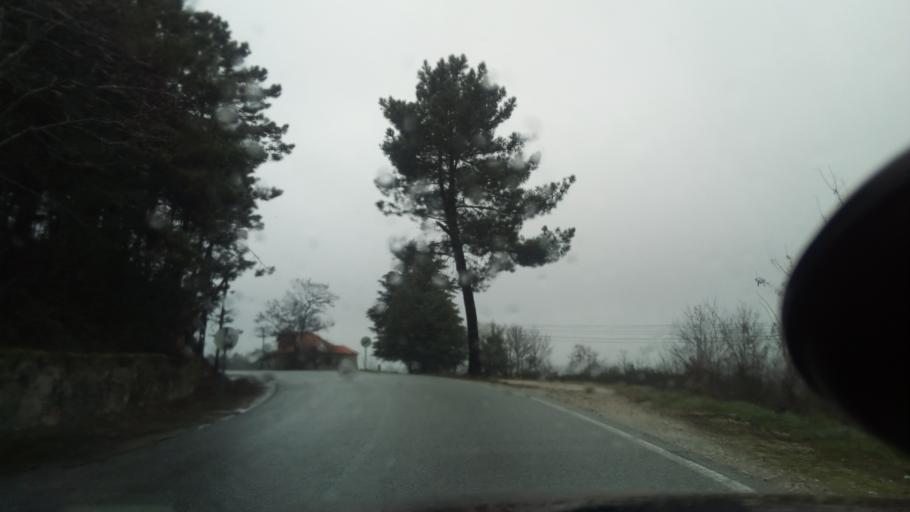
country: PT
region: Viseu
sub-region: Mangualde
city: Mangualde
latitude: 40.6107
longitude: -7.6573
